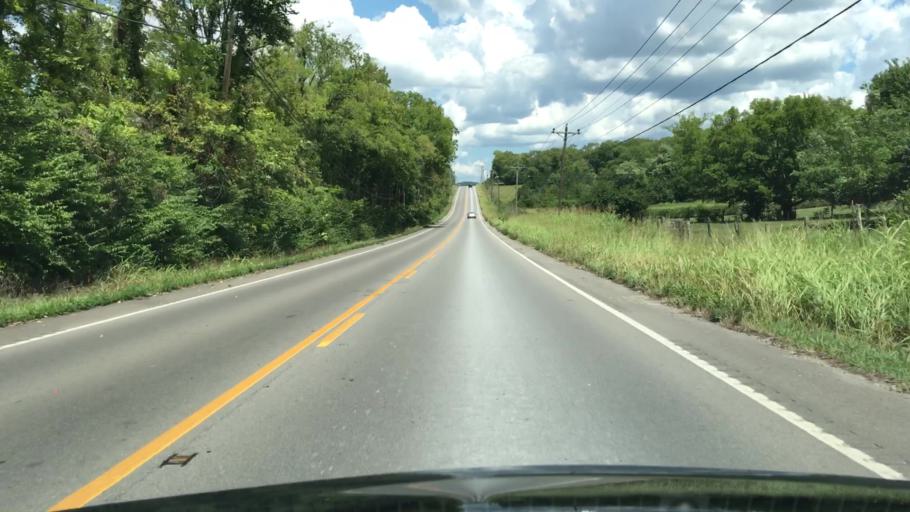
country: US
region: Tennessee
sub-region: Williamson County
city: Nolensville
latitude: 35.8676
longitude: -86.6595
